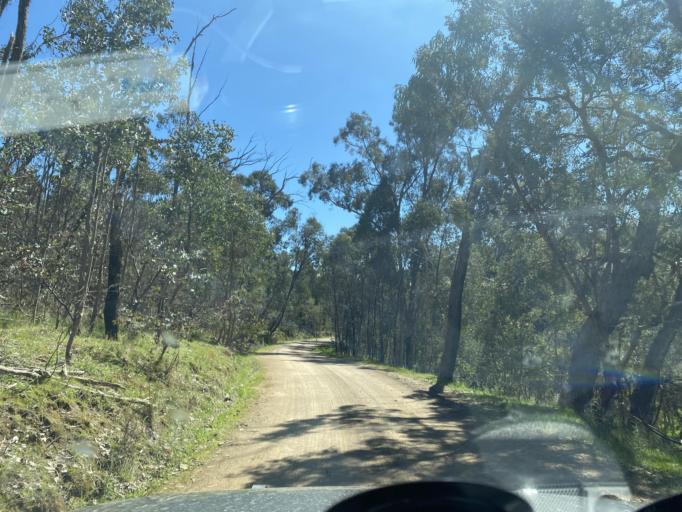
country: AU
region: Victoria
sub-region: Benalla
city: Benalla
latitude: -36.7040
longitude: 146.1783
